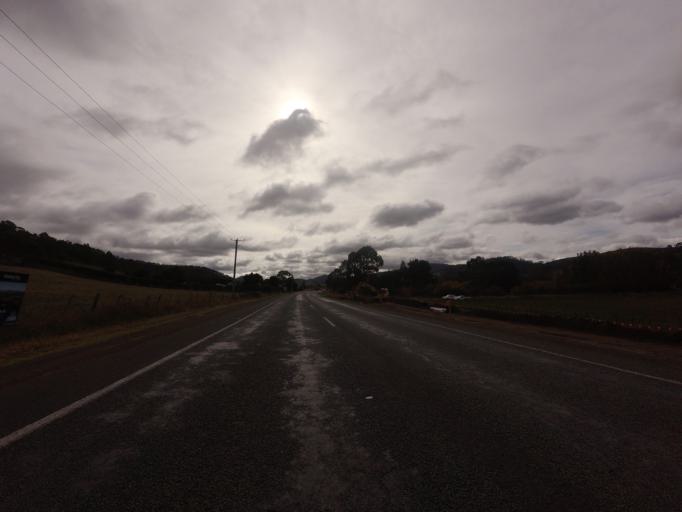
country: AU
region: Tasmania
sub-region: Brighton
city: Bridgewater
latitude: -42.6219
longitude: 147.2222
